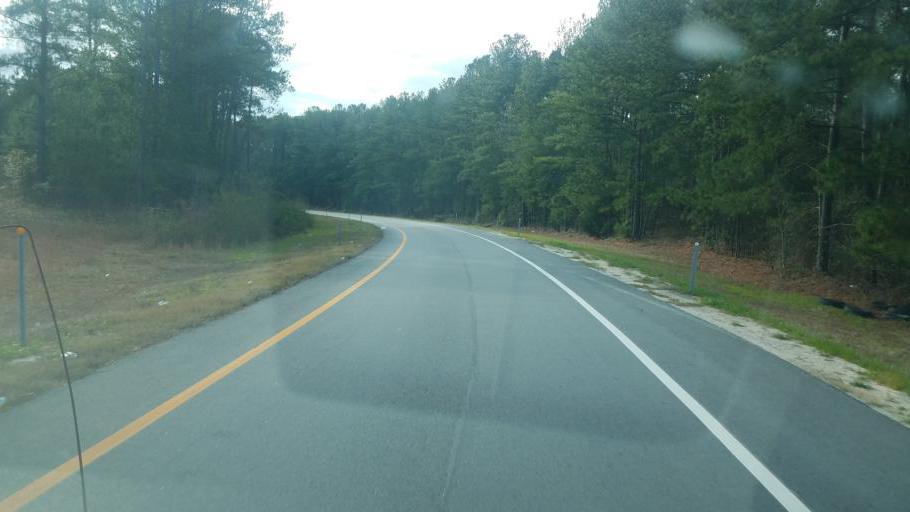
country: US
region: South Carolina
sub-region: Richland County
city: Dentsville
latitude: 34.0964
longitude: -80.9576
